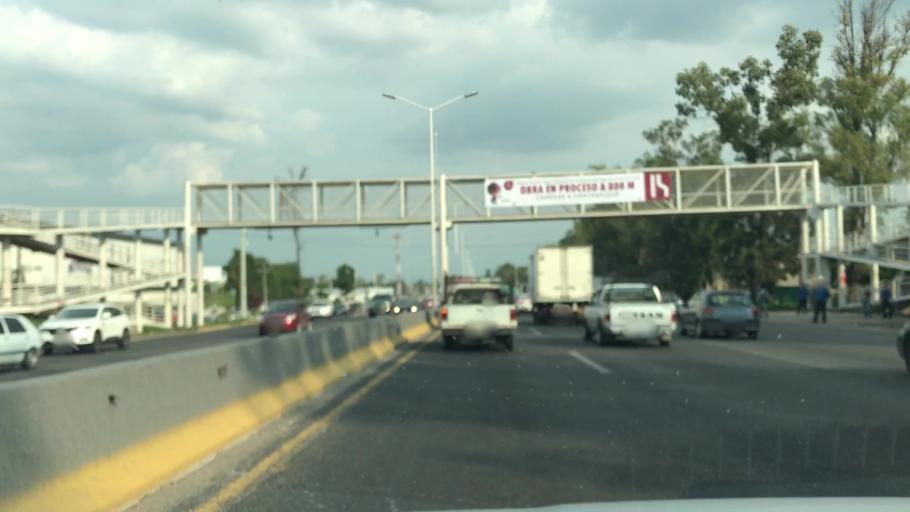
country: MX
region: Jalisco
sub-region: Tlajomulco de Zuniga
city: La Tijera
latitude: 20.6212
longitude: -103.4306
